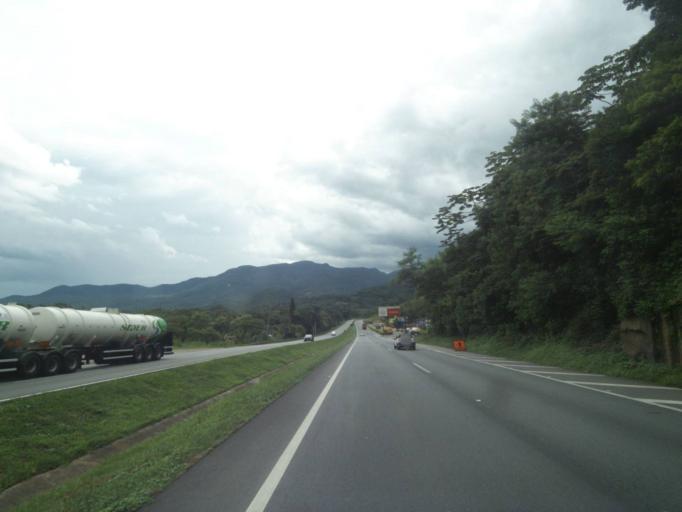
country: BR
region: Parana
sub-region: Antonina
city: Antonina
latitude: -25.5564
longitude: -48.8041
